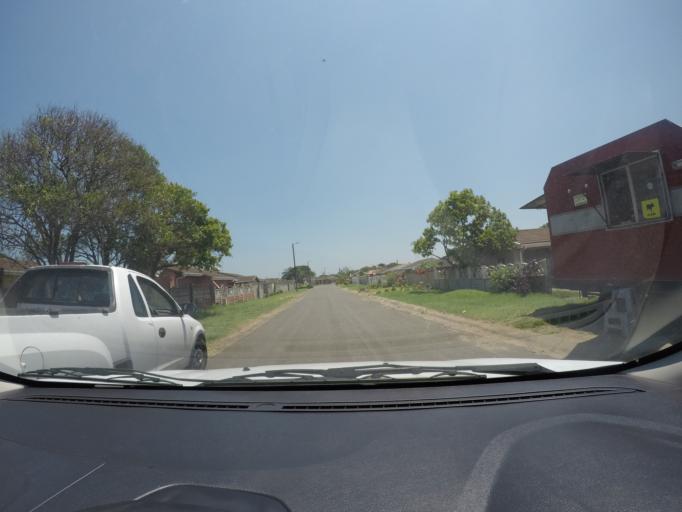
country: ZA
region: KwaZulu-Natal
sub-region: uThungulu District Municipality
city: eSikhawini
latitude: -28.8877
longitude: 31.8904
